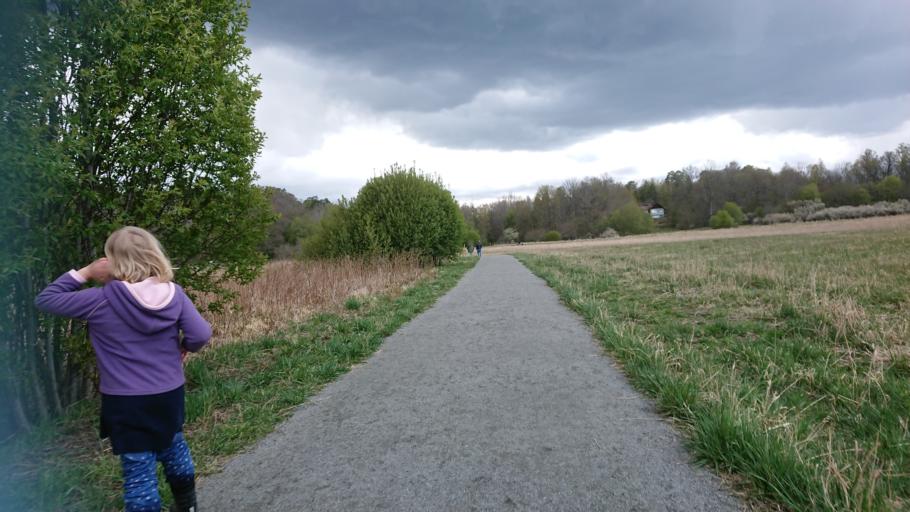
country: SE
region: Uppsala
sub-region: Uppsala Kommun
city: Uppsala
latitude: 59.7973
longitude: 17.6091
